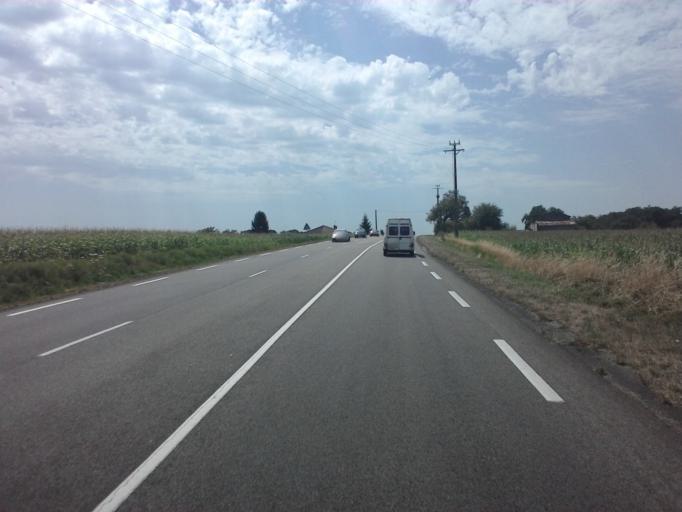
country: FR
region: Rhone-Alpes
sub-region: Departement de l'Ain
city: Saint-Etienne-du-Bois
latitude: 46.3086
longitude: 5.3038
